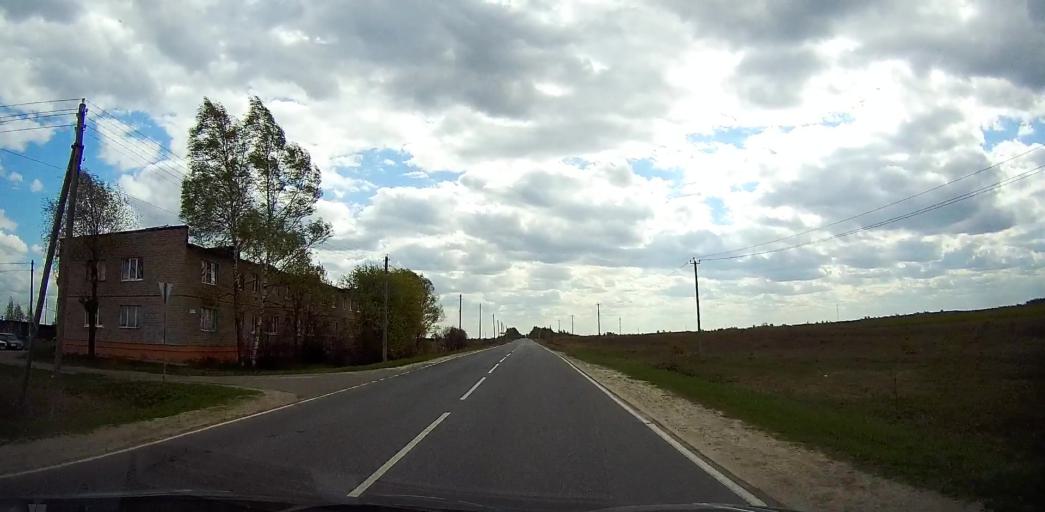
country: RU
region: Moskovskaya
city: Davydovo
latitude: 55.6429
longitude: 38.7499
